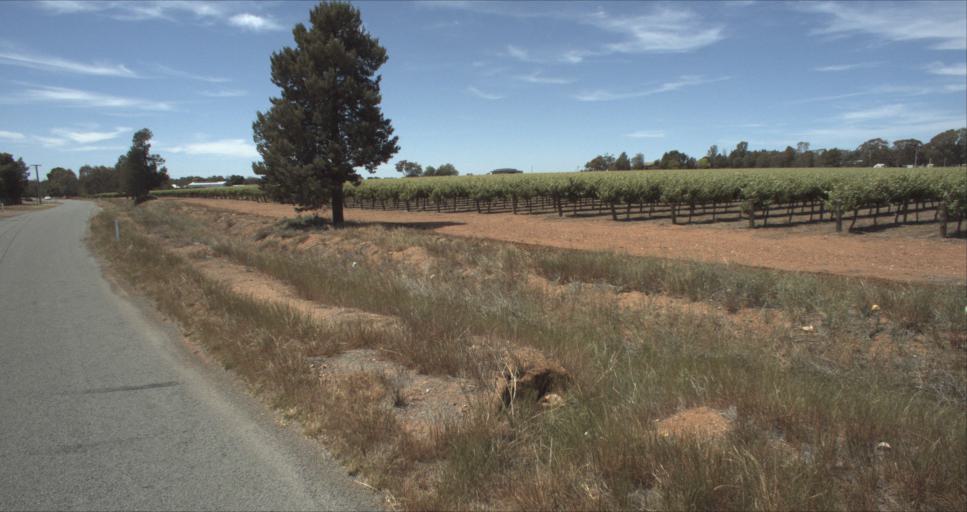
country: AU
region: New South Wales
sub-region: Leeton
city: Leeton
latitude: -34.5680
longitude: 146.4448
